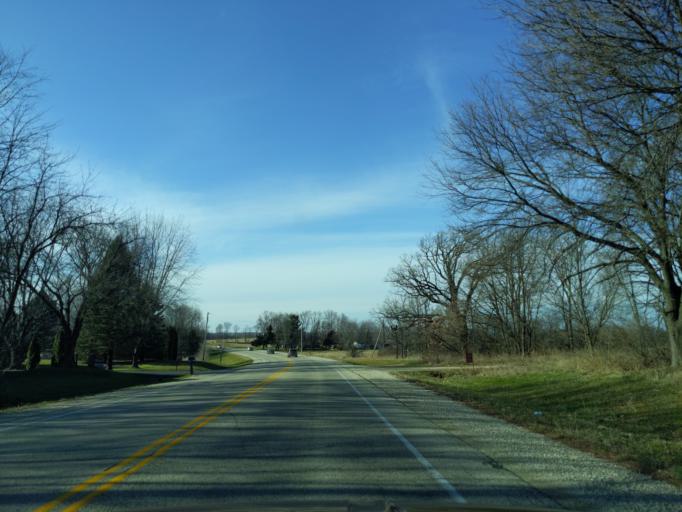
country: US
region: Wisconsin
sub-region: Rock County
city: Milton
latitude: 42.8239
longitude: -88.9595
